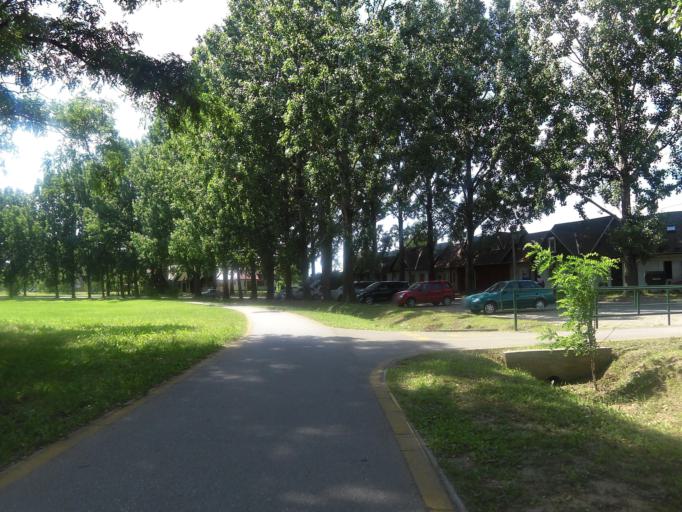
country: HU
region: Jasz-Nagykun-Szolnok
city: Tiszafured
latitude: 47.6245
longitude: 20.7355
